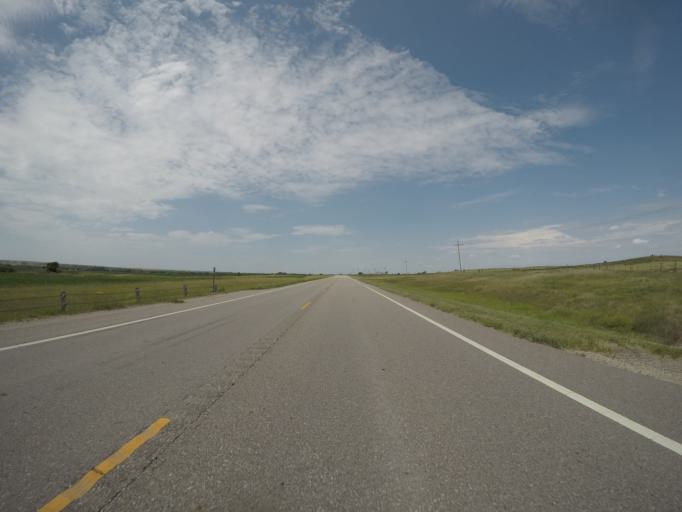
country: US
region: Kansas
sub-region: Rooks County
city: Stockton
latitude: 39.4442
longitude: -99.2054
